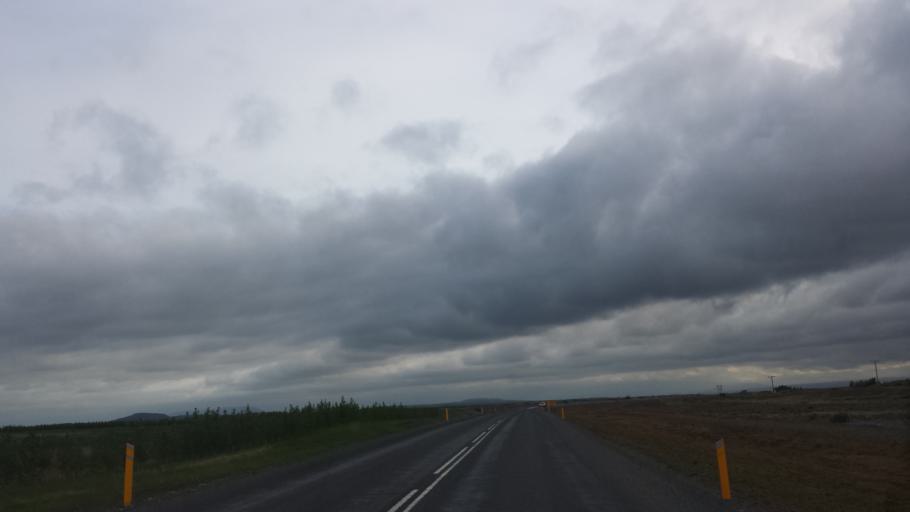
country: IS
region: South
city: Selfoss
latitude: 64.2758
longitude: -20.3515
